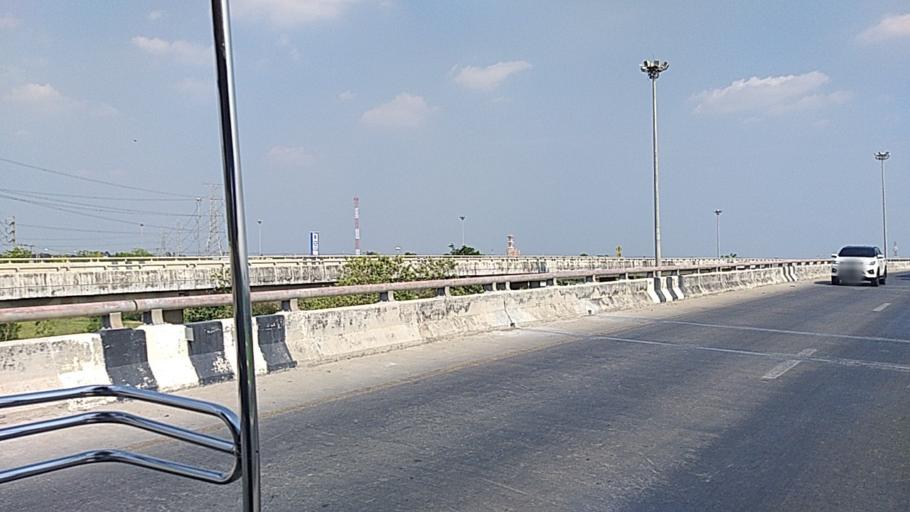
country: TH
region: Pathum Thani
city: Sam Khok
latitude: 14.0947
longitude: 100.5177
